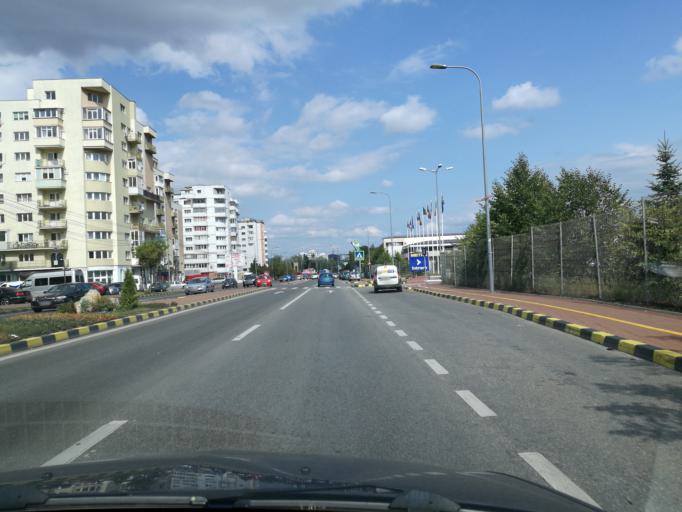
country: RO
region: Suceava
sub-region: Comuna Scheia
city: Scheia
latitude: 47.6355
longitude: 26.2345
